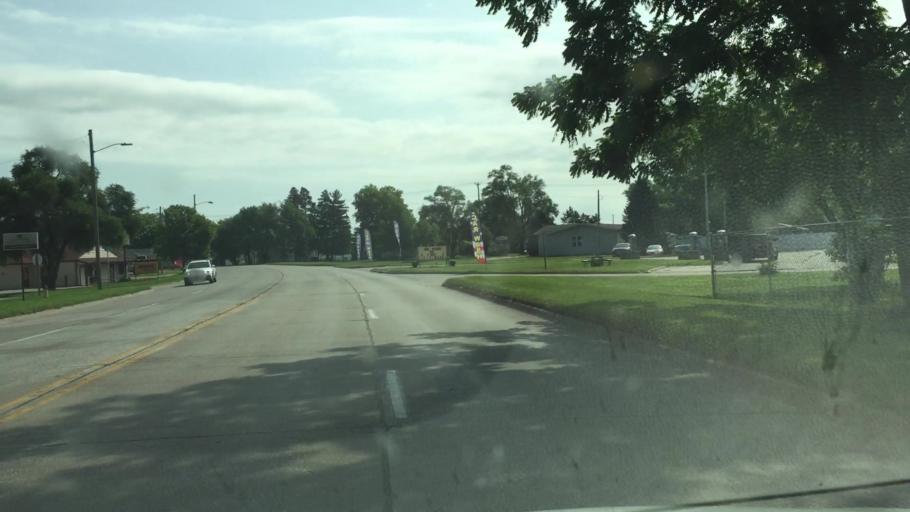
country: US
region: Iowa
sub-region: Lee County
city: Fort Madison
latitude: 40.6245
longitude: -91.3609
